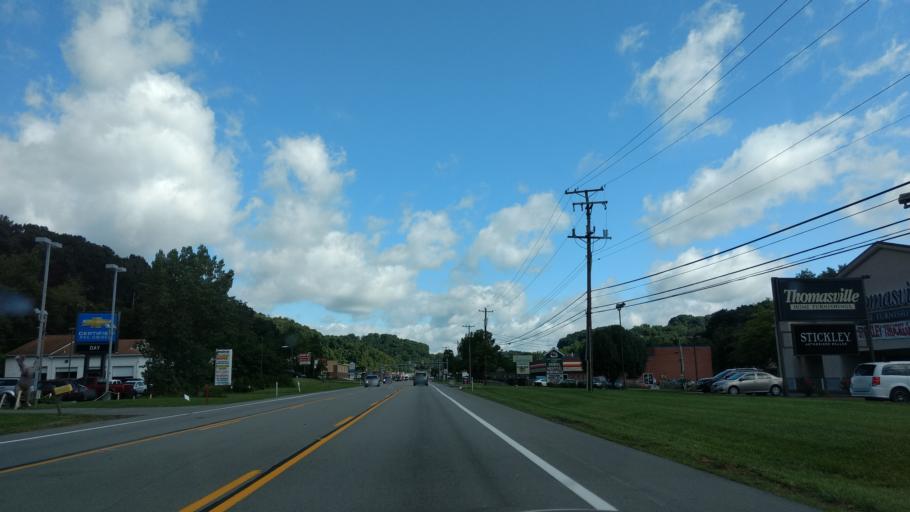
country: US
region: Pennsylvania
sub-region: Westmoreland County
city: Murrysville
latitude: 40.4398
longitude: -79.7130
